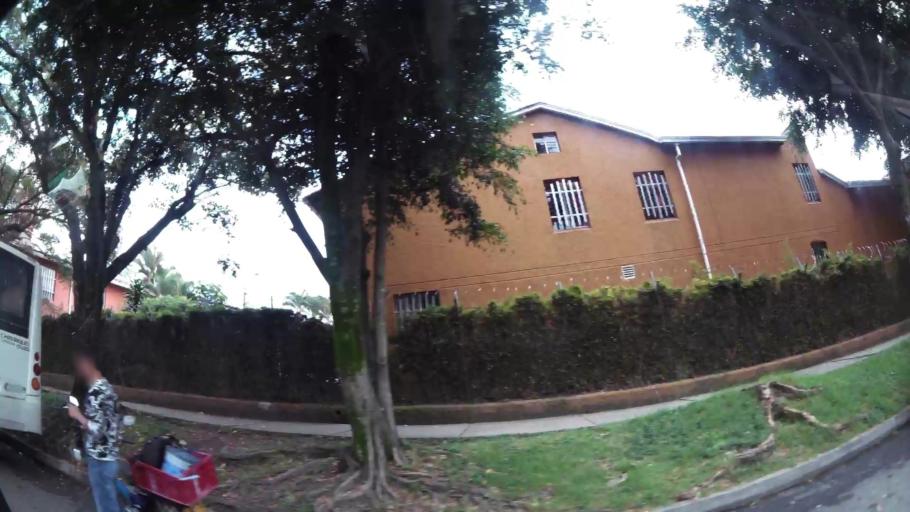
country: CO
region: Antioquia
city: Medellin
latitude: 6.2451
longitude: -75.6203
